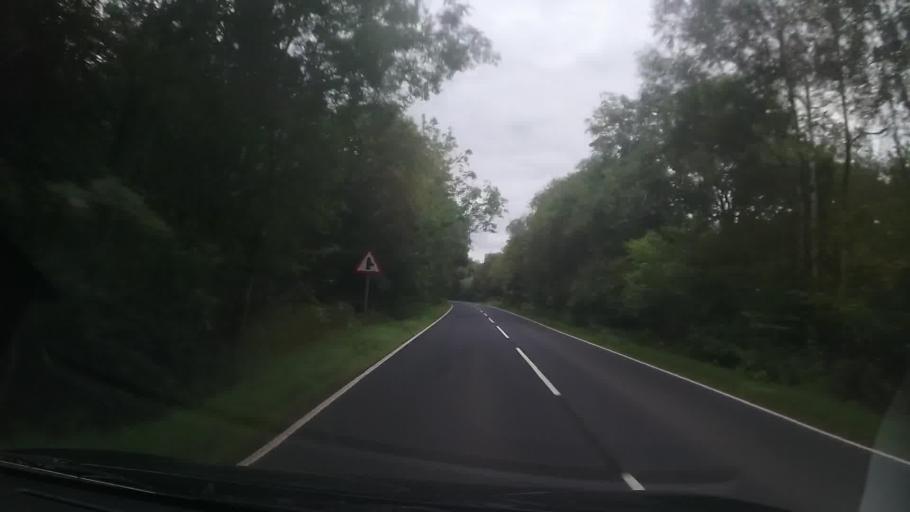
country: GB
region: Scotland
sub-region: Argyll and Bute
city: Garelochhead
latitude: 56.2033
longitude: -5.0612
